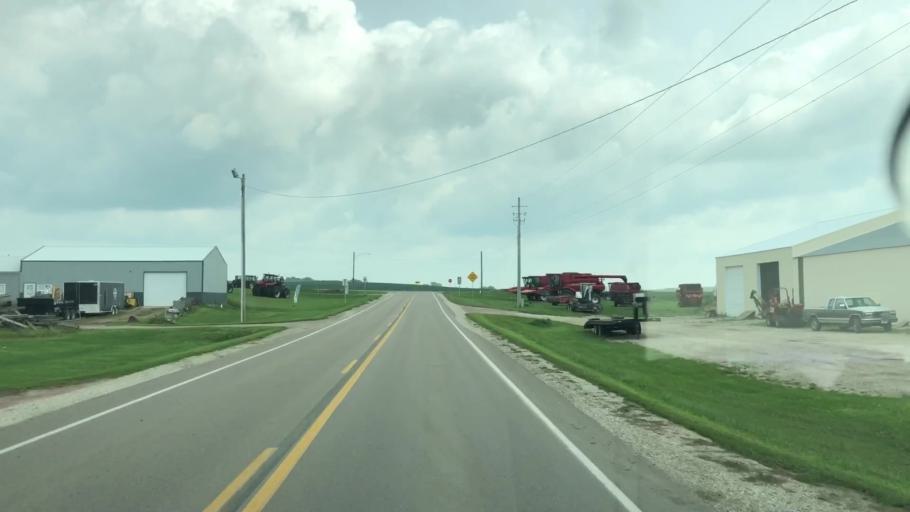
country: US
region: Iowa
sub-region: Plymouth County
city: Kingsley
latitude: 42.5866
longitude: -95.9599
